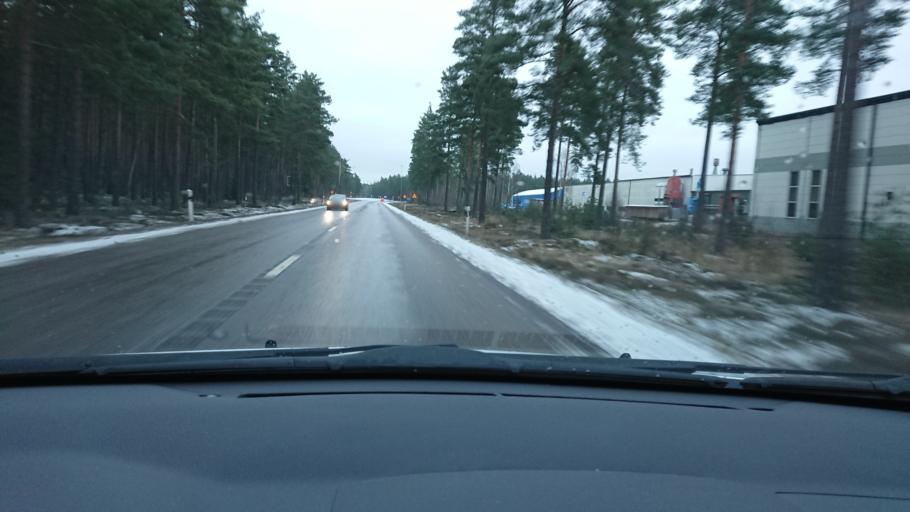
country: SE
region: Kalmar
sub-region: Hultsfreds Kommun
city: Hultsfred
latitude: 57.5083
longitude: 15.8325
